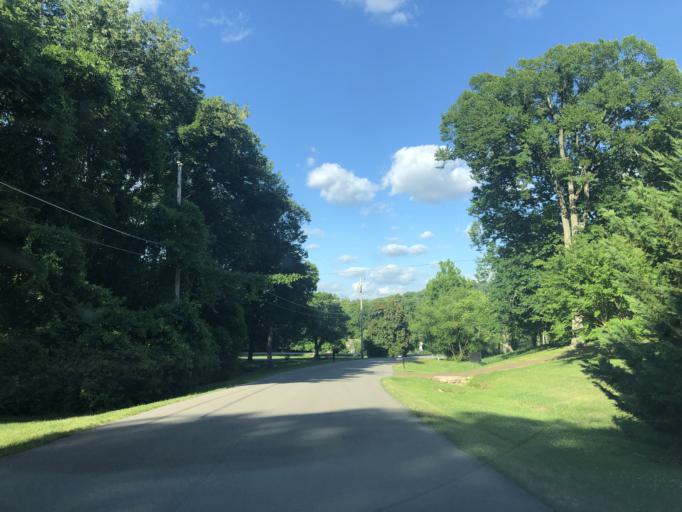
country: US
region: Tennessee
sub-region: Davidson County
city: Forest Hills
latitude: 36.0876
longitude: -86.8217
